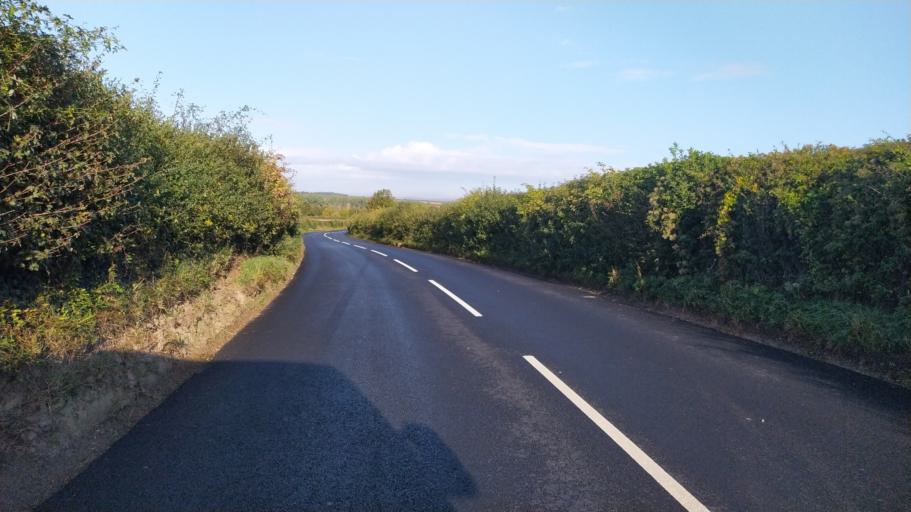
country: GB
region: England
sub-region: Dorset
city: Three Legged Cross
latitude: 50.8741
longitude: -1.9712
